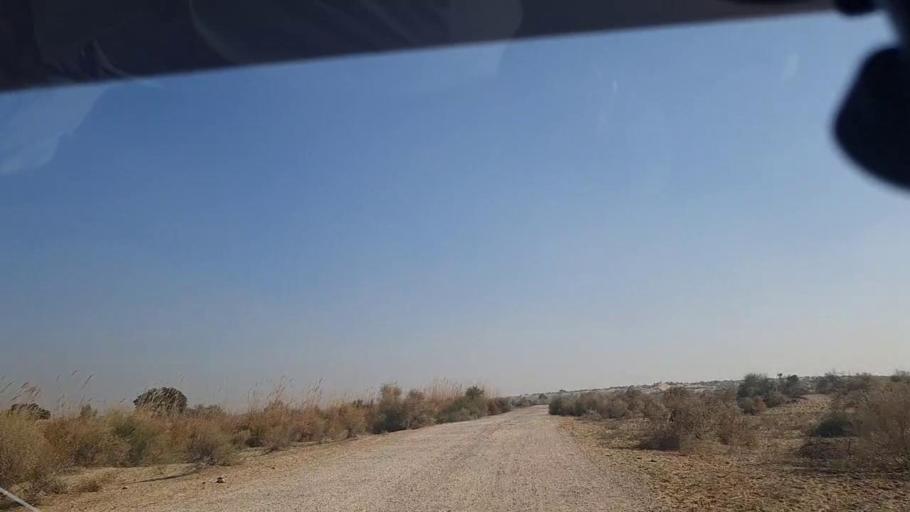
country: PK
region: Sindh
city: Khanpur
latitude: 27.5631
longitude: 69.3218
